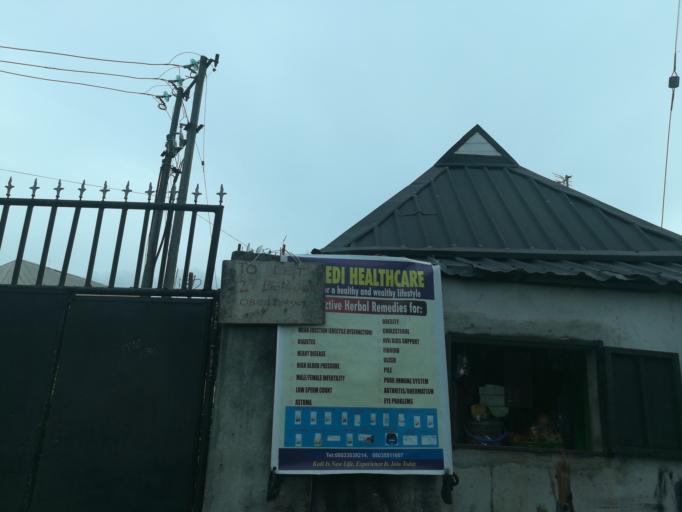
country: NG
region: Rivers
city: Port Harcourt
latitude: 4.8087
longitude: 6.9978
